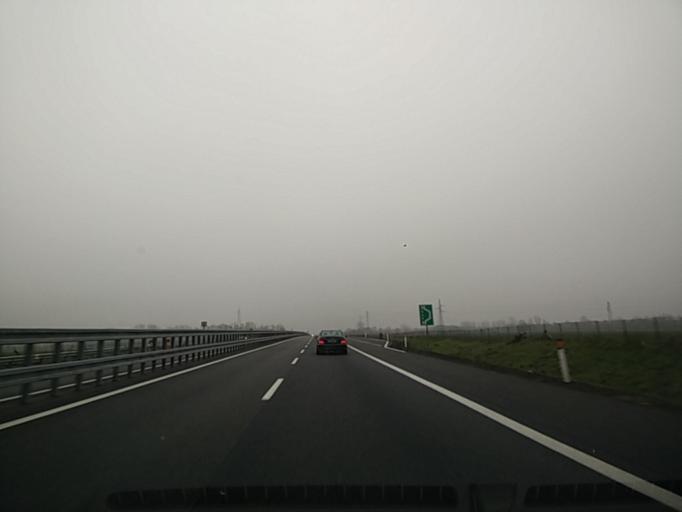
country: IT
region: Piedmont
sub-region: Provincia di Alessandria
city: Solero
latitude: 44.9241
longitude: 8.4937
